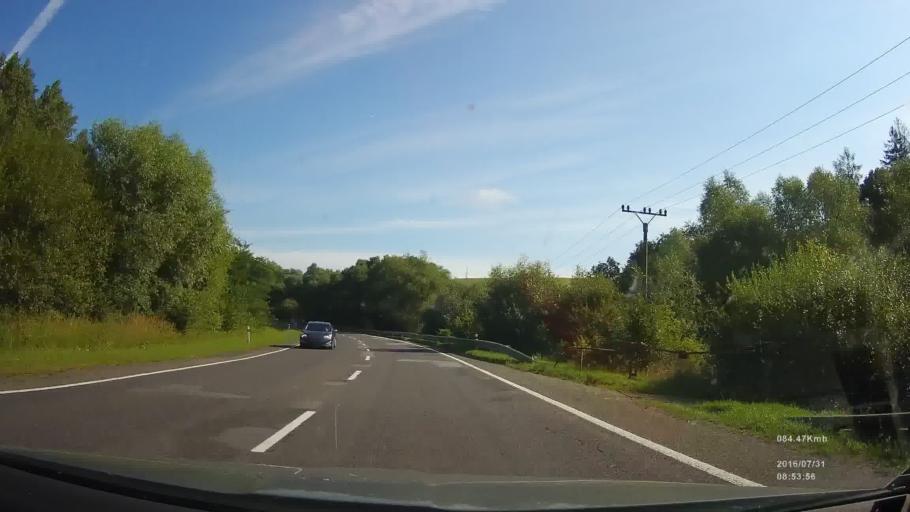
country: SK
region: Presovsky
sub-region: Okres Presov
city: Presov
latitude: 49.1311
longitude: 21.3167
